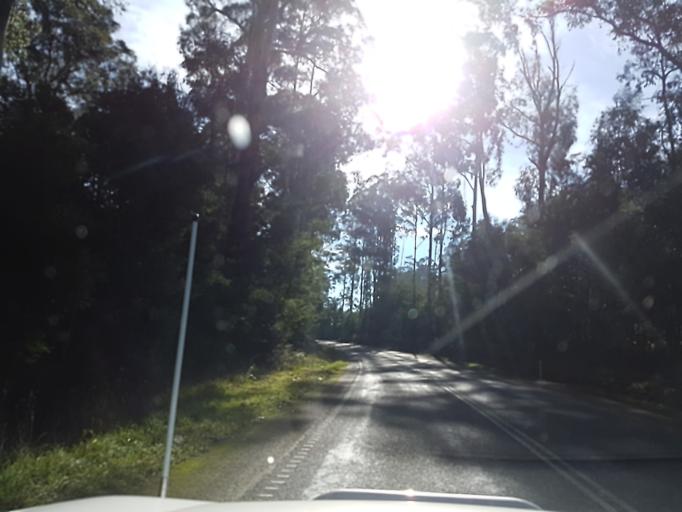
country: AU
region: Victoria
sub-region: Yarra Ranges
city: Yarra Glen
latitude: -37.5131
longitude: 145.4251
